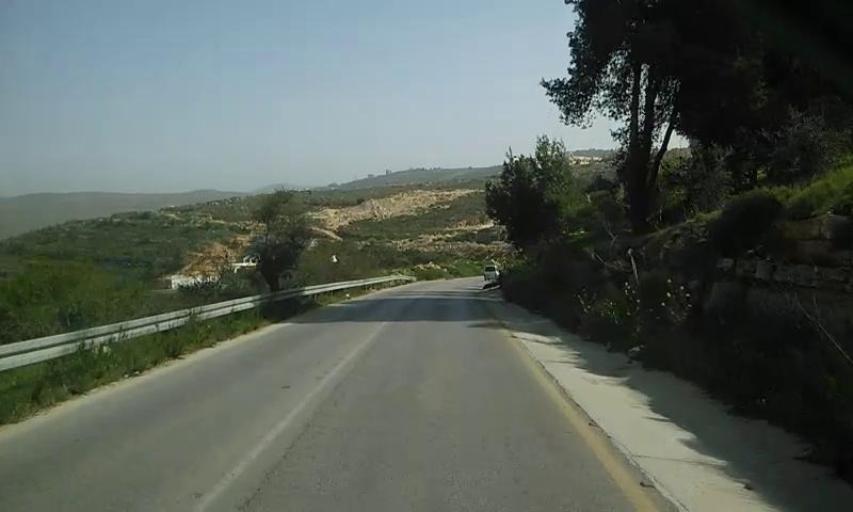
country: PS
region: West Bank
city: Dura al Qar`
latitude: 31.9632
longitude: 35.2260
